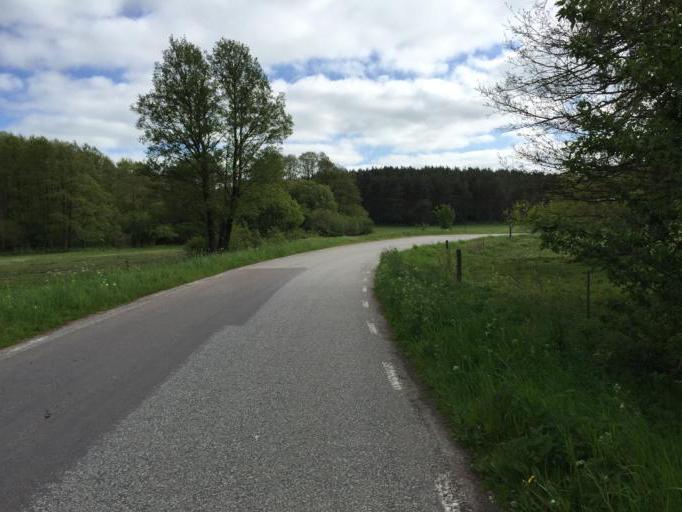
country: SE
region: Skane
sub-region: Sjobo Kommun
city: Blentarp
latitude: 55.6624
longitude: 13.6173
